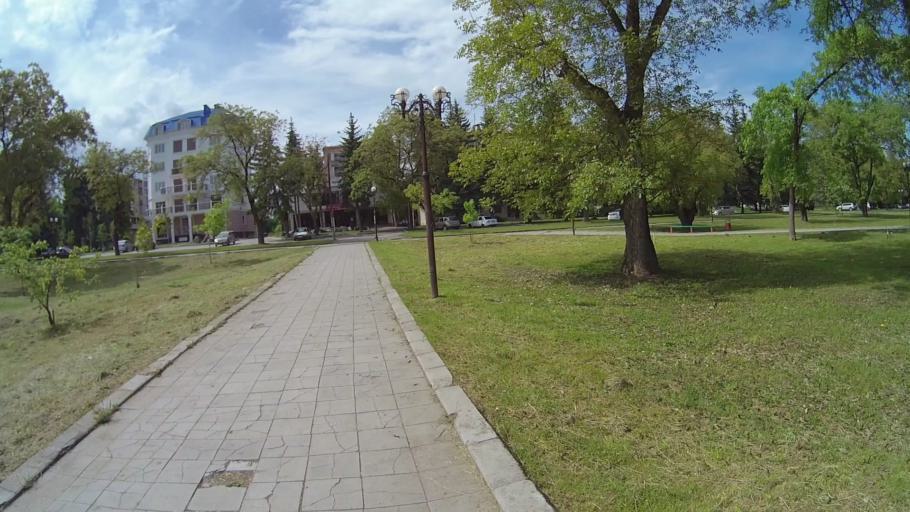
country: RU
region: Kabardino-Balkariya
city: Kenzhe
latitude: 43.4769
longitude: 43.5851
